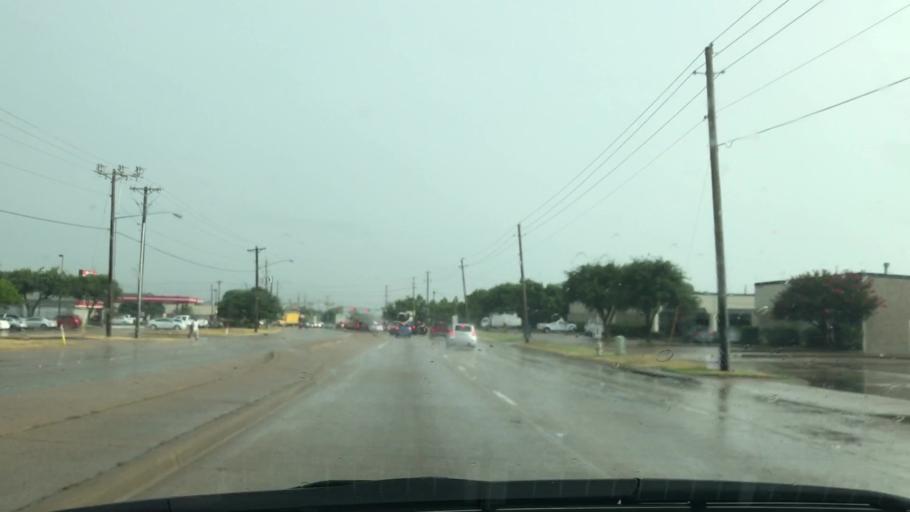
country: US
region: Texas
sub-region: Dallas County
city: Richardson
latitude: 32.8967
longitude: -96.7006
